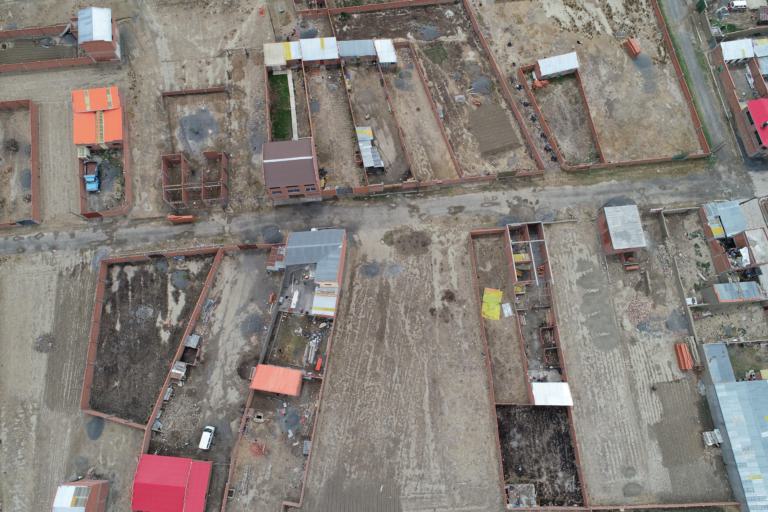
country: BO
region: La Paz
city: Achacachi
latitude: -16.0516
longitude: -68.6845
